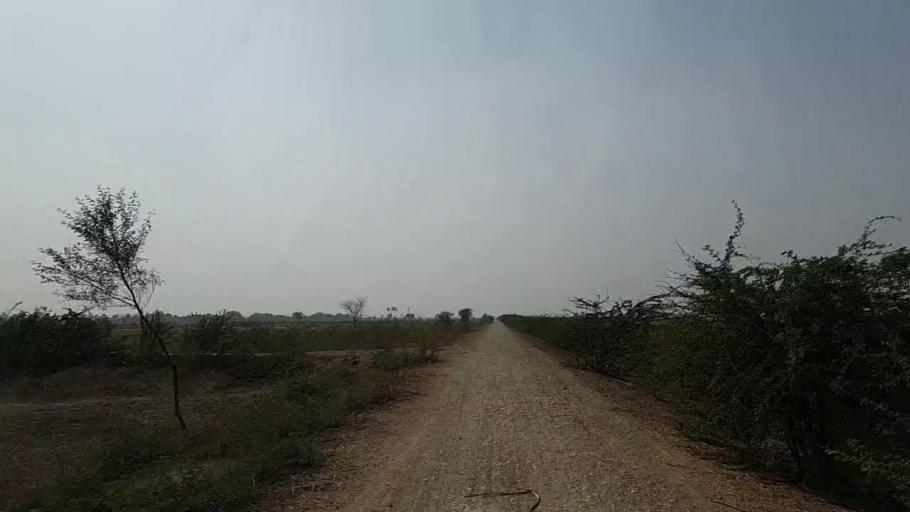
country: PK
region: Sindh
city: Naukot
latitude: 24.7605
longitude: 69.3317
